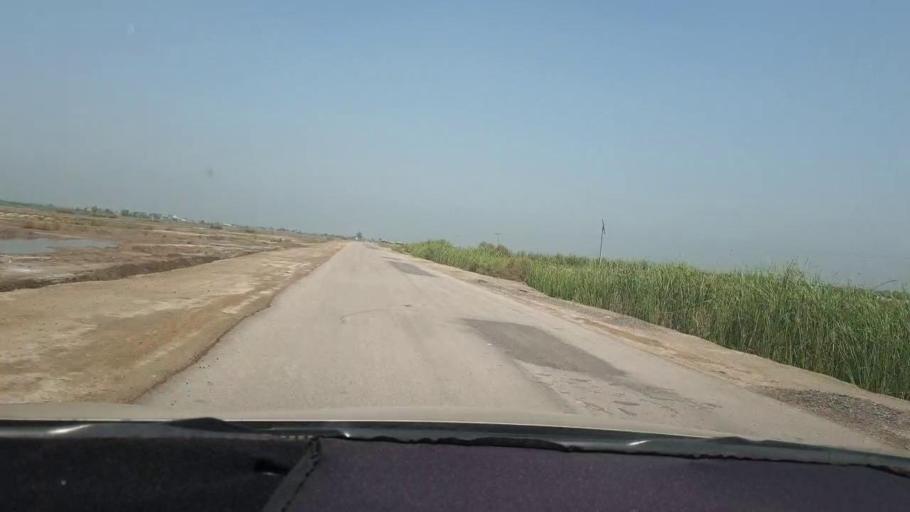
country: PK
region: Sindh
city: Miro Khan
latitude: 27.8309
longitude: 68.0150
